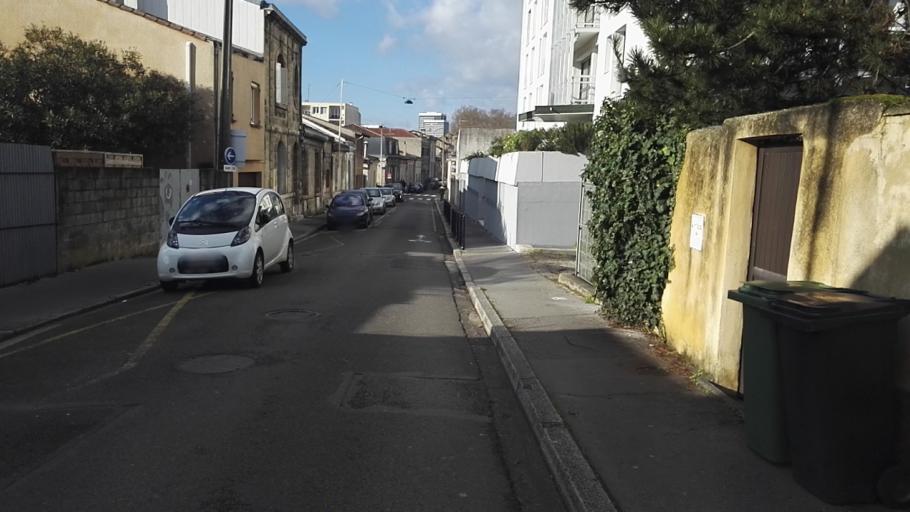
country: FR
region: Aquitaine
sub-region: Departement de la Gironde
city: Bordeaux
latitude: 44.8308
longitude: -0.5928
